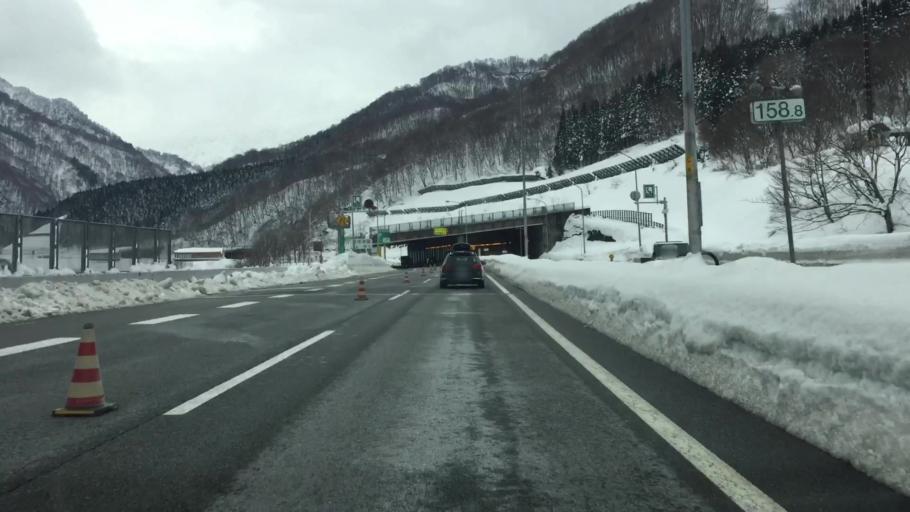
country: JP
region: Niigata
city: Shiozawa
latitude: 36.8725
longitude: 138.8646
